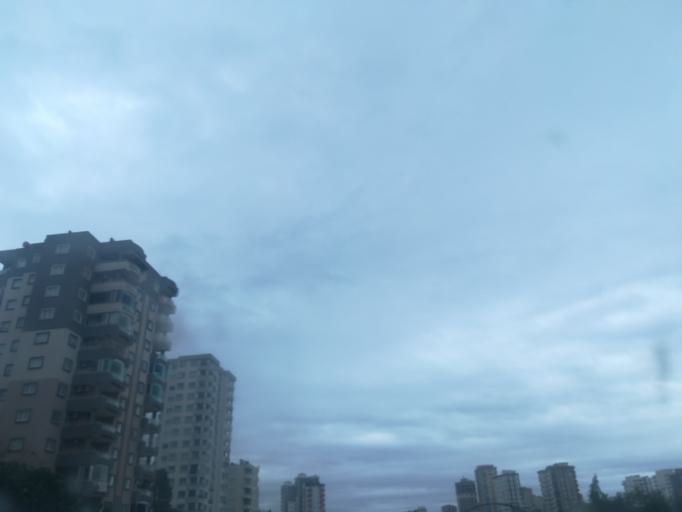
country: TR
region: Adana
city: Seyhan
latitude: 37.0319
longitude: 35.2832
